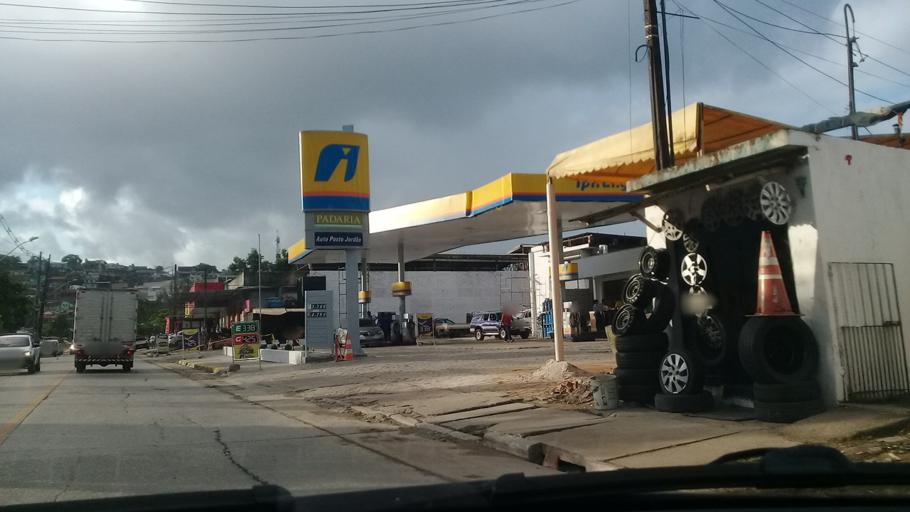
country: BR
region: Pernambuco
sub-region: Jaboatao Dos Guararapes
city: Jaboatao
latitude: -8.1386
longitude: -34.9359
